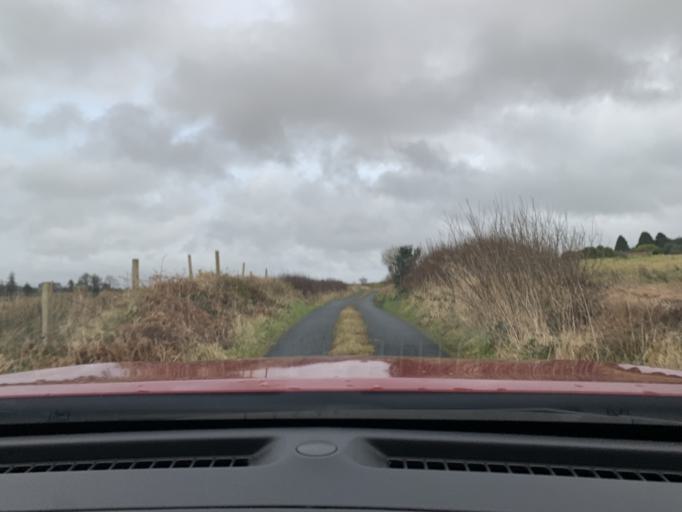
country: IE
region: Connaught
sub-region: Roscommon
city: Boyle
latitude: 53.9921
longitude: -8.4082
